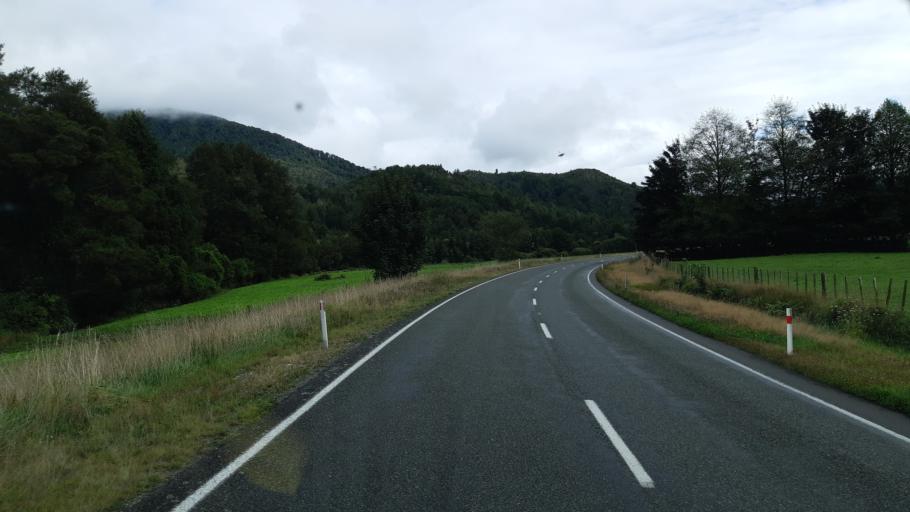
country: NZ
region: West Coast
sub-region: Buller District
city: Westport
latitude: -41.8083
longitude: 172.2187
